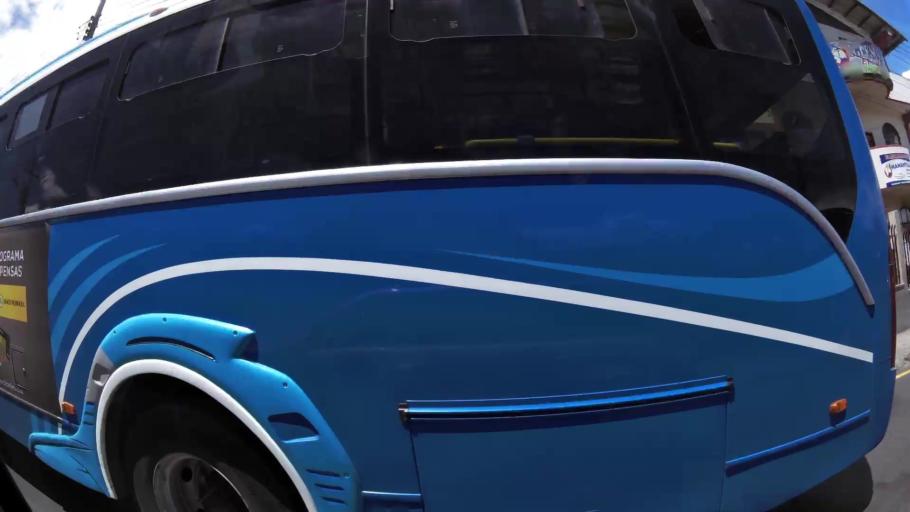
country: EC
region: Tungurahua
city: Ambato
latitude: -1.2758
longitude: -78.6279
